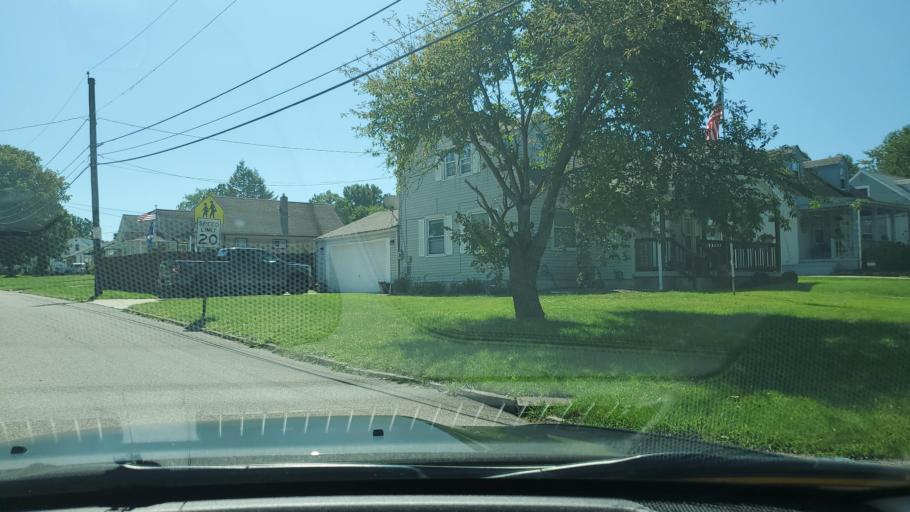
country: US
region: Ohio
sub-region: Mahoning County
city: Struthers
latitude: 41.0586
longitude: -80.6102
